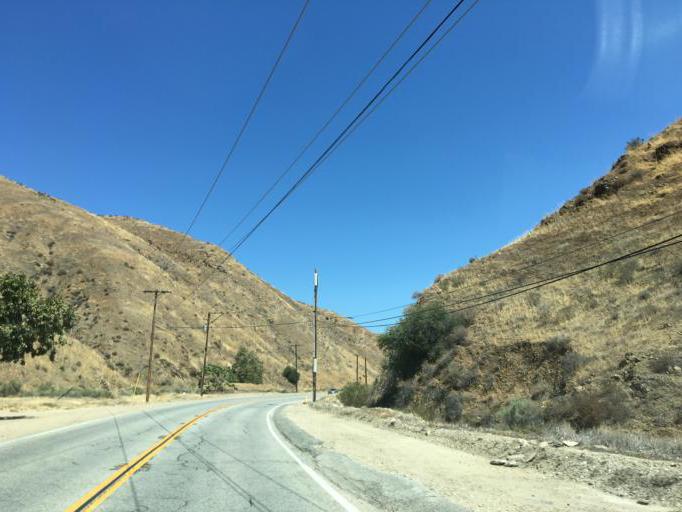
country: US
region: California
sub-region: Los Angeles County
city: Agua Dulce
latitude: 34.4902
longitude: -118.3870
